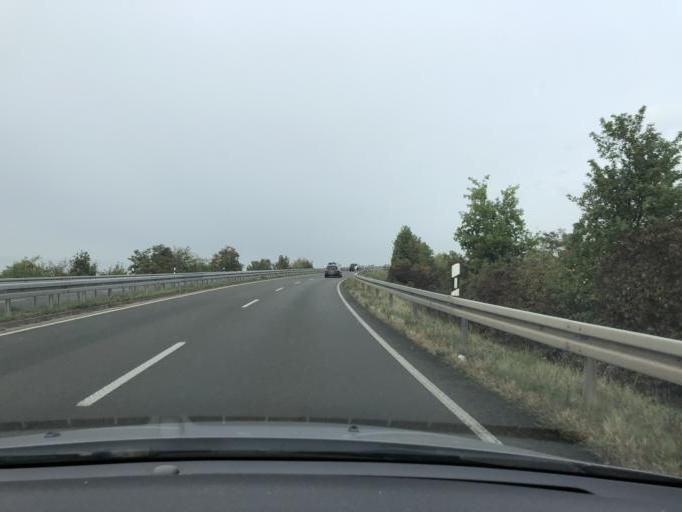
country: DE
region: Saxony
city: Schkeuditz
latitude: 51.3870
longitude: 12.2979
